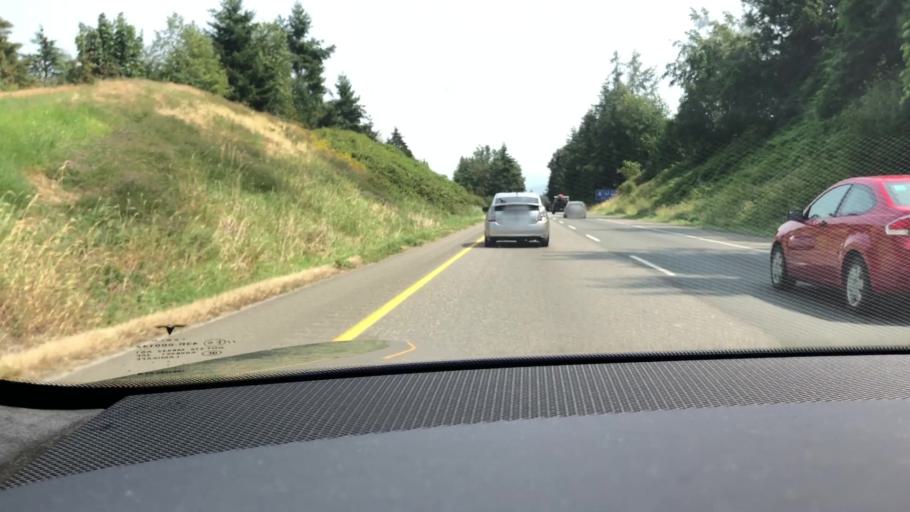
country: US
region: Washington
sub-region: Whatcom County
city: Sumas
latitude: 49.0437
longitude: -122.3494
